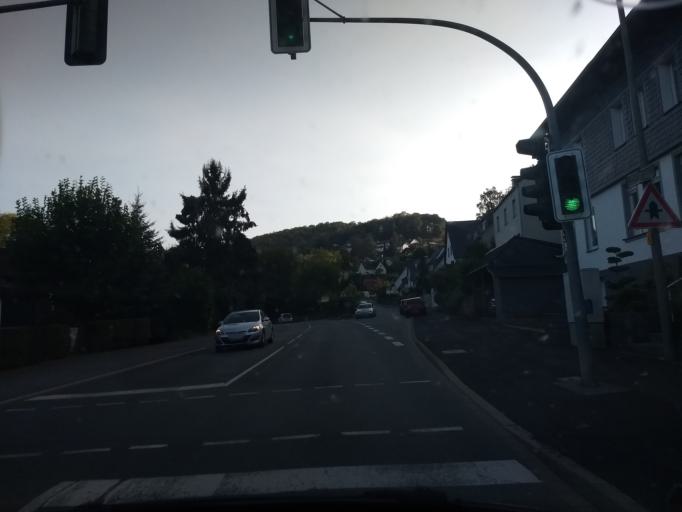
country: DE
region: North Rhine-Westphalia
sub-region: Regierungsbezirk Arnsberg
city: Arnsberg
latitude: 51.3956
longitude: 8.0552
